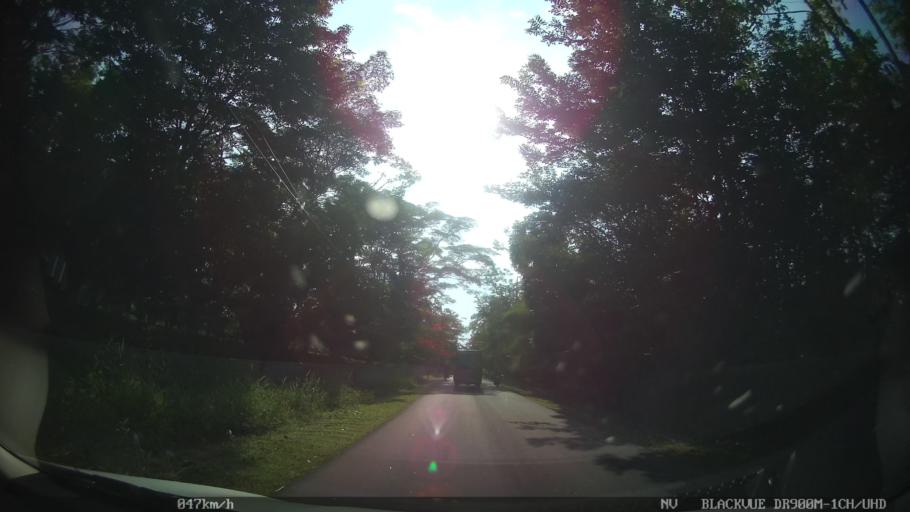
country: ID
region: North Sumatra
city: Percut
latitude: 3.5933
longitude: 98.8034
